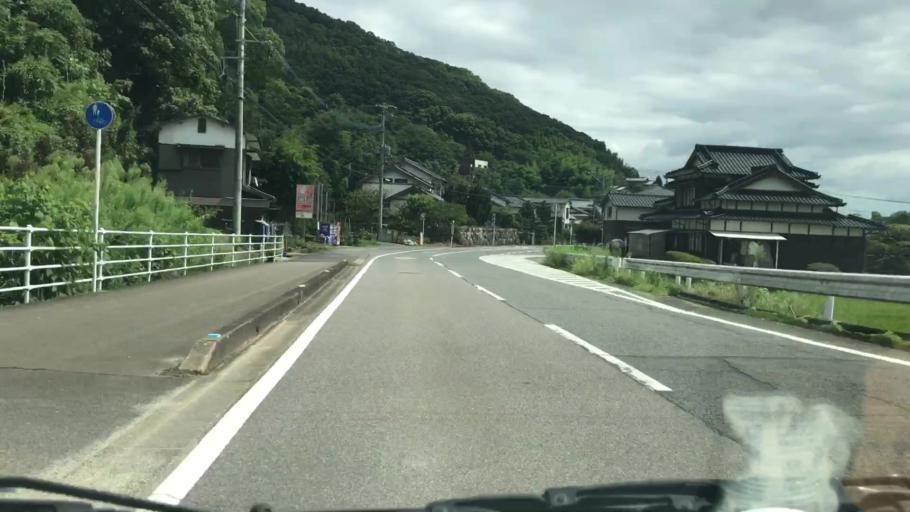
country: JP
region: Saga Prefecture
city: Kashima
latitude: 33.2259
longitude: 130.1551
